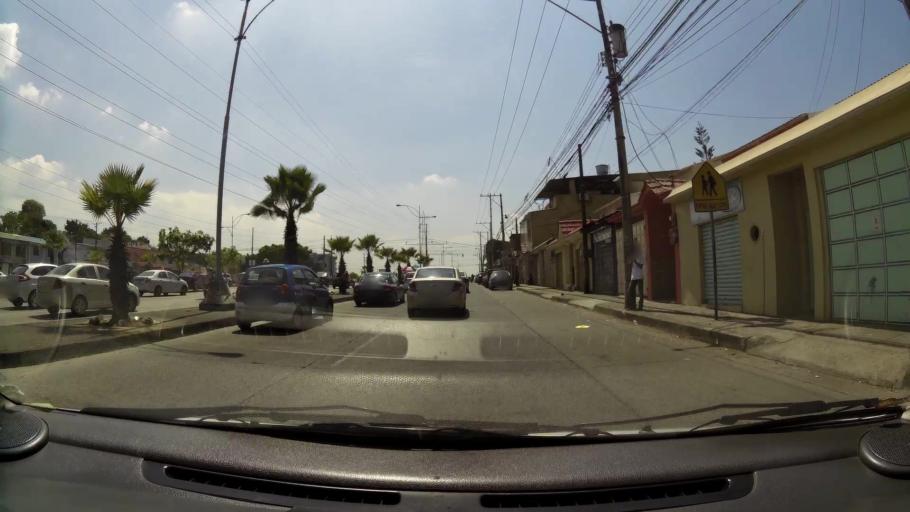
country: EC
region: Guayas
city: Eloy Alfaro
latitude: -2.1105
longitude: -79.9079
